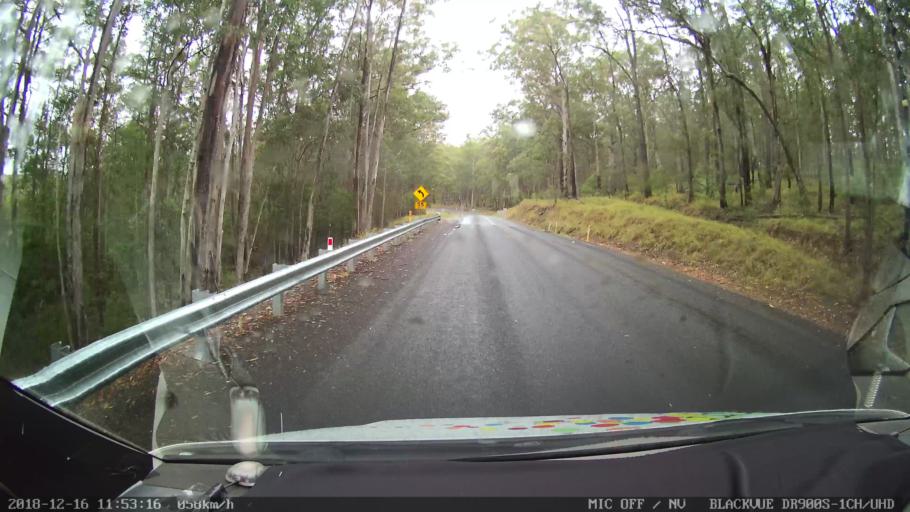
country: AU
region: New South Wales
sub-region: Tenterfield Municipality
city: Carrolls Creek
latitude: -28.9044
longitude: 152.2778
